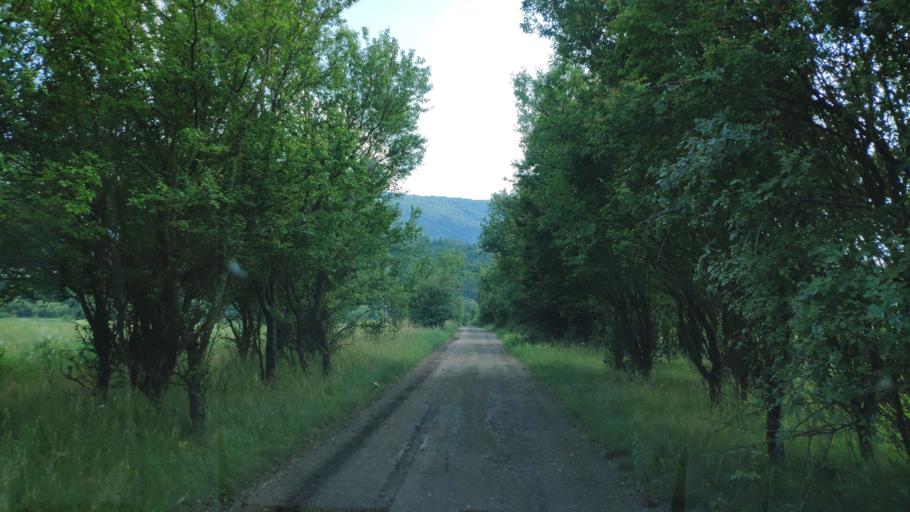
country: HU
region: Borsod-Abauj-Zemplen
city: Szendro
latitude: 48.5934
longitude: 20.7296
